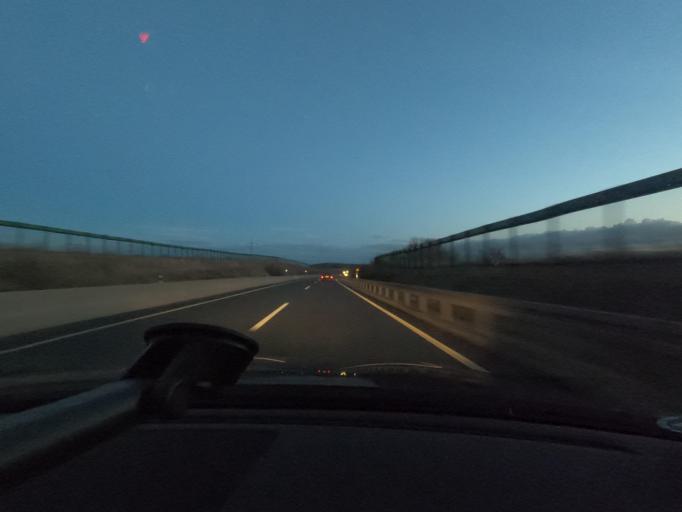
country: DE
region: Lower Saxony
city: Bad Sachsa
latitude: 51.5864
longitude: 10.5080
